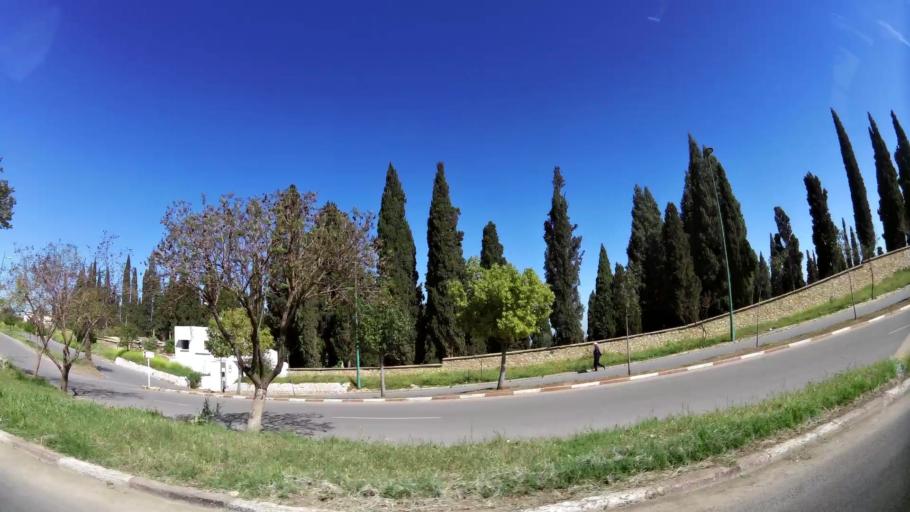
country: MA
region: Meknes-Tafilalet
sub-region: Meknes
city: Meknes
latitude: 33.9073
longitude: -5.5464
